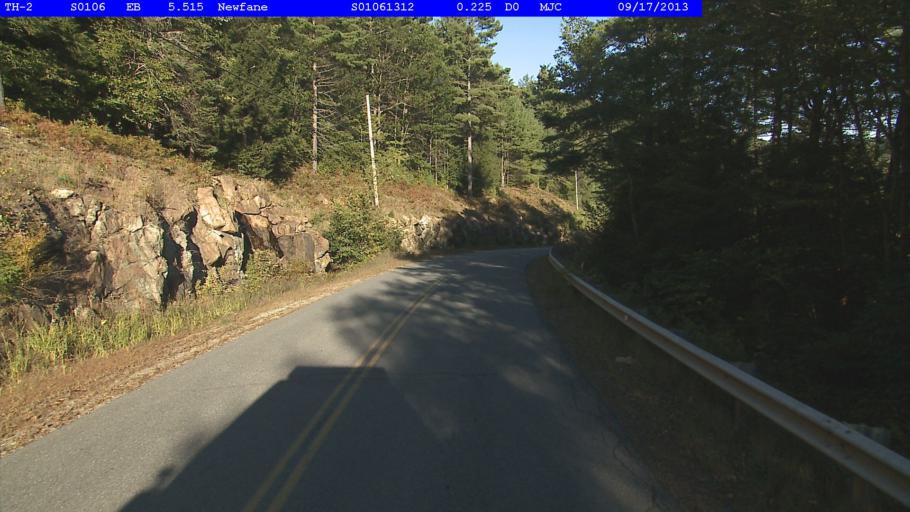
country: US
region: Vermont
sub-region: Windham County
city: Dover
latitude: 42.9501
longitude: -72.7614
